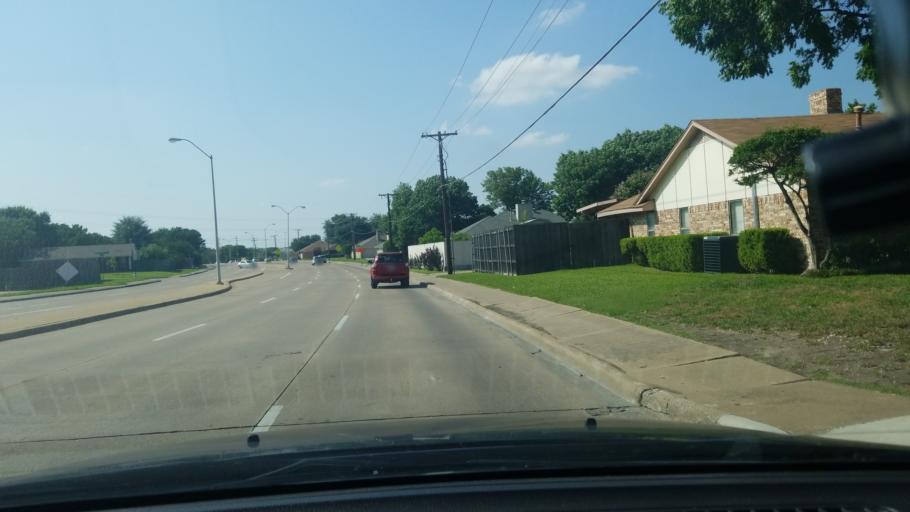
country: US
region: Texas
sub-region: Dallas County
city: Mesquite
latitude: 32.8138
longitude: -96.6115
